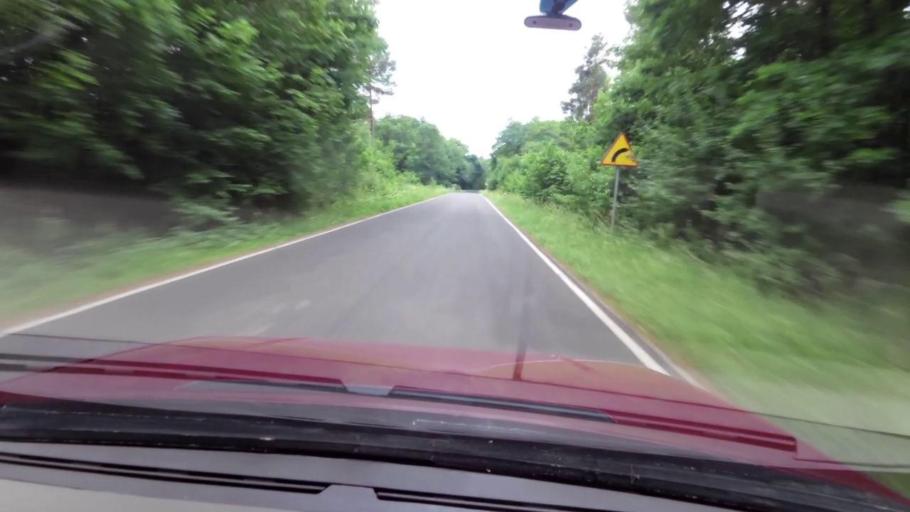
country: PL
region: West Pomeranian Voivodeship
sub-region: Powiat koszalinski
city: Polanow
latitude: 54.1516
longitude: 16.6941
